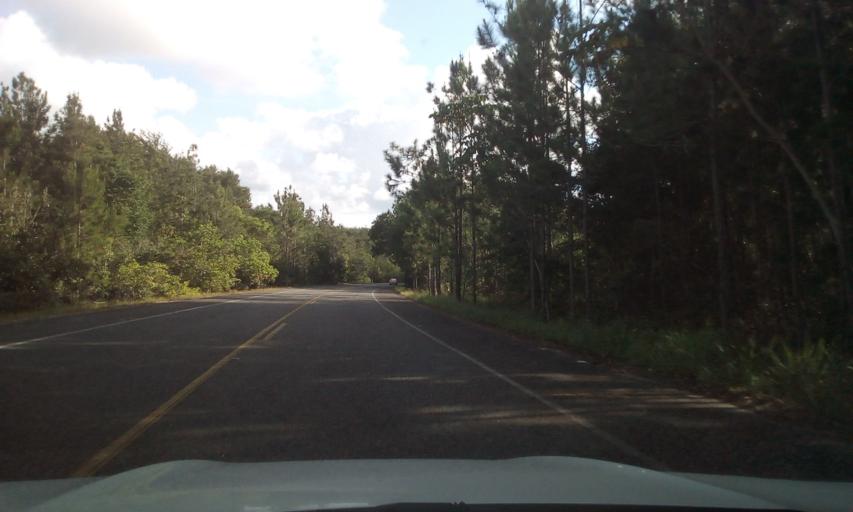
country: BR
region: Bahia
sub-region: Conde
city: Conde
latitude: -12.1030
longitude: -37.7820
